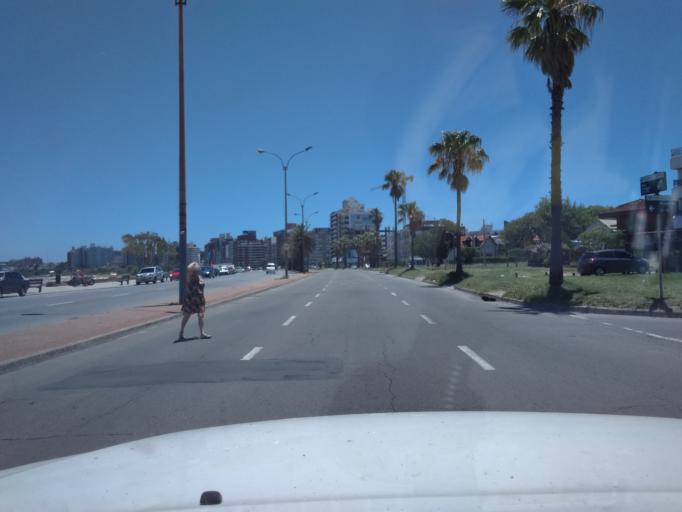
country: UY
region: Canelones
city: Paso de Carrasco
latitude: -34.8970
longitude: -56.1021
